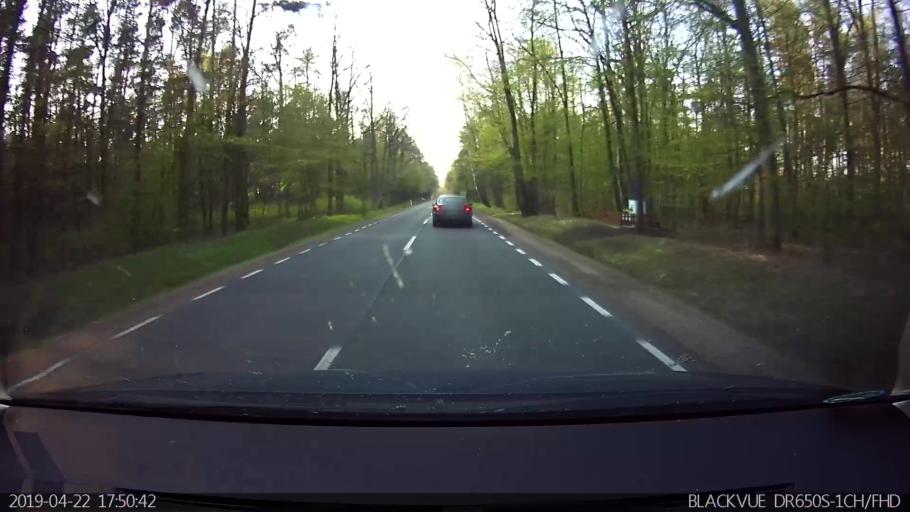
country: PL
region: Masovian Voivodeship
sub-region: Powiat wegrowski
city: Wegrow
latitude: 52.4279
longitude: 21.9997
